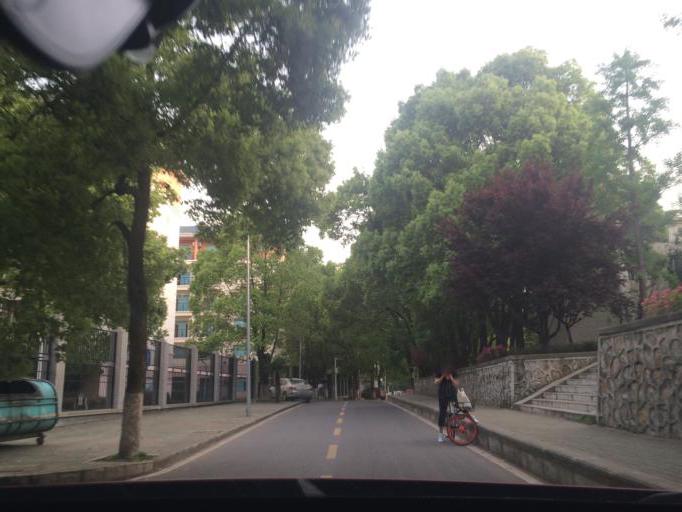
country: CN
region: Hubei
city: Guanshan
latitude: 30.5311
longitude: 114.3576
